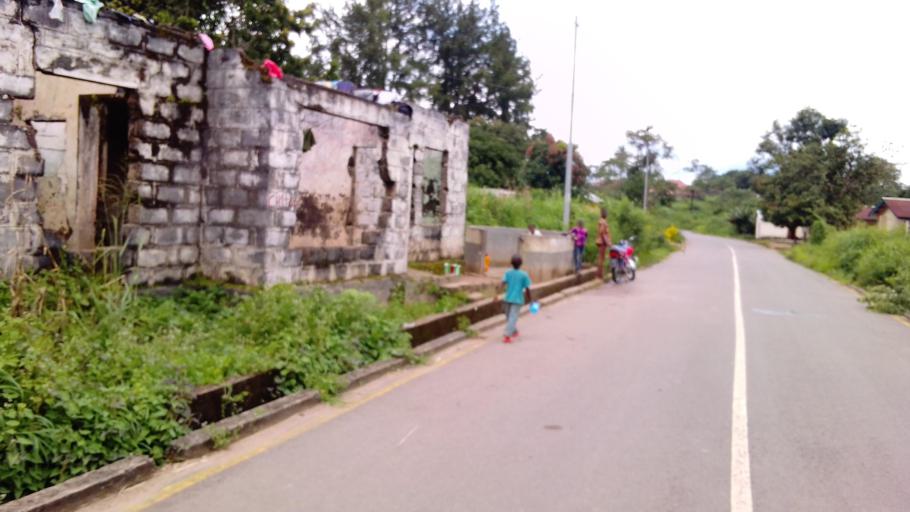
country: SL
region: Eastern Province
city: Koidu
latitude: 8.6567
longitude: -10.9855
